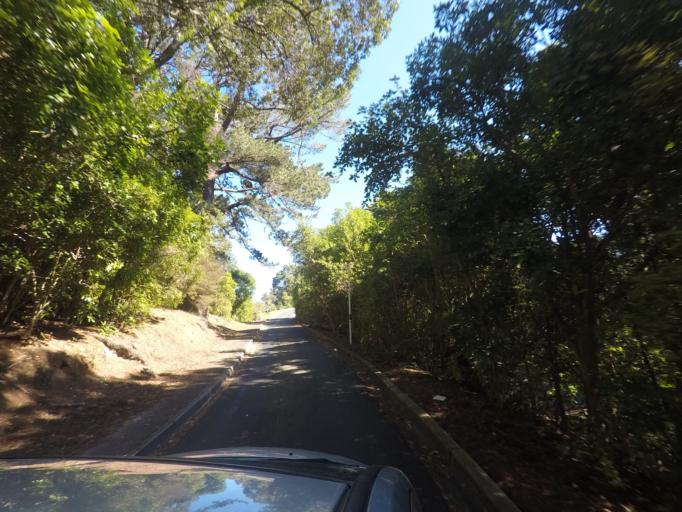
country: NZ
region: Auckland
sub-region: Auckland
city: Titirangi
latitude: -36.9316
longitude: 174.6986
